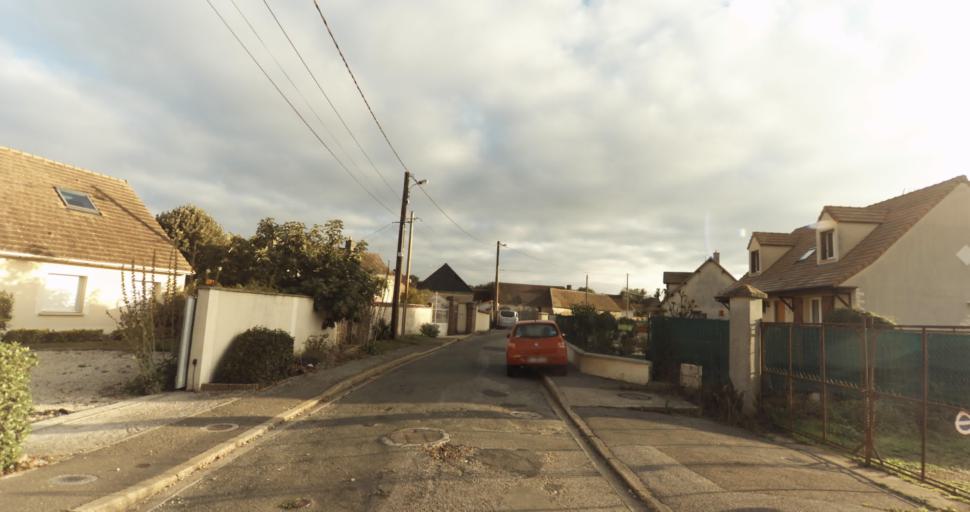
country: FR
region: Centre
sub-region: Departement d'Eure-et-Loir
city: Vernouillet
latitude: 48.7162
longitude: 1.3814
